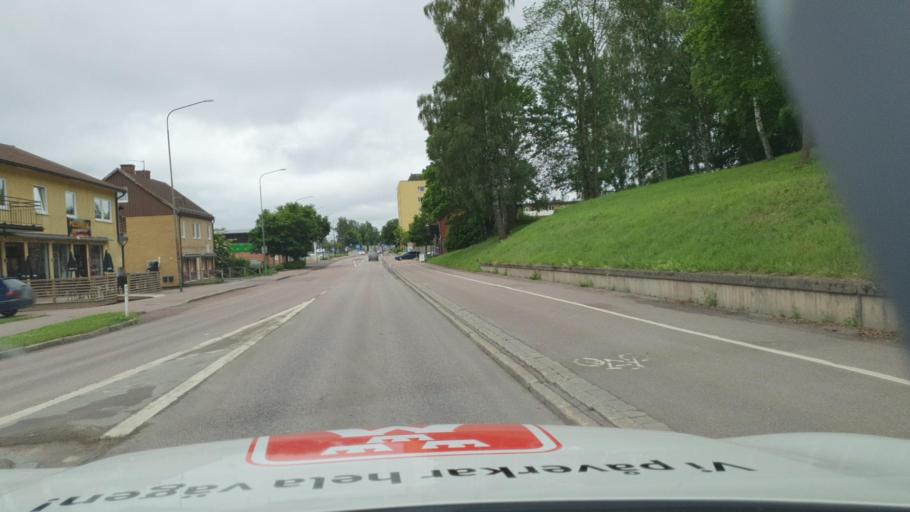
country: SE
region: Vaermland
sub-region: Grums Kommun
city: Grums
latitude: 59.3551
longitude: 13.1136
